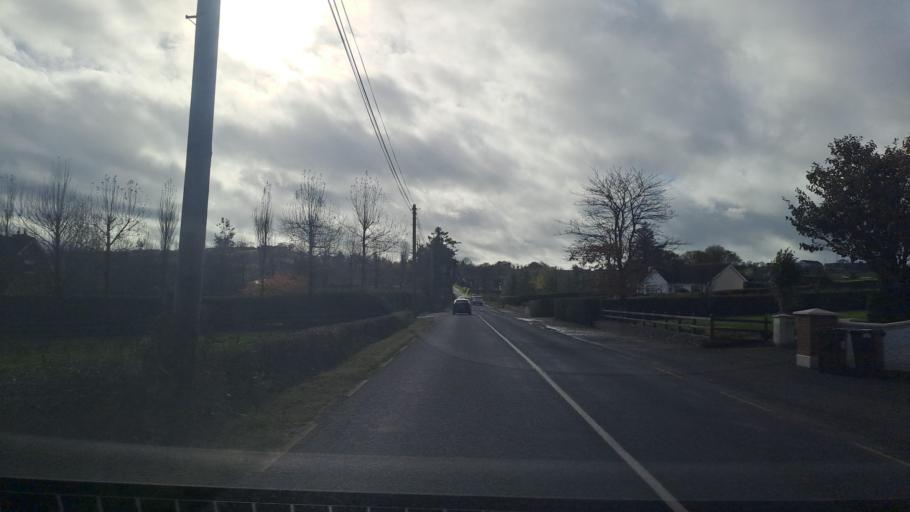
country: IE
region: Ulster
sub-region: County Monaghan
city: Monaghan
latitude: 54.1988
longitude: -6.9887
